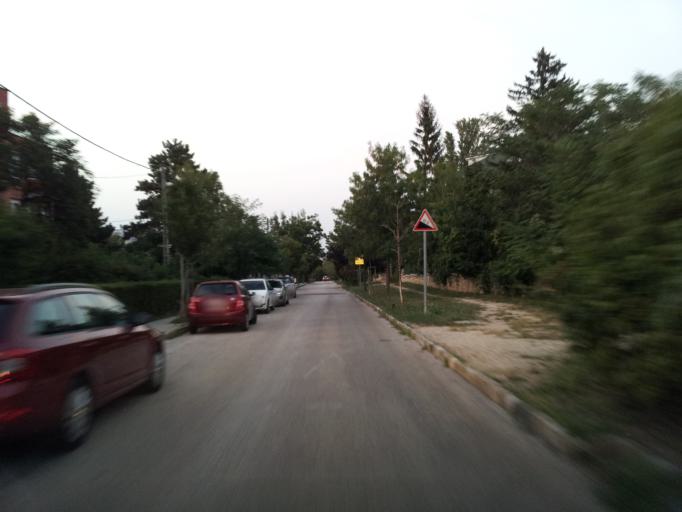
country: HU
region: Budapest
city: Budapest XII. keruelet
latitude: 47.4849
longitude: 19.0098
